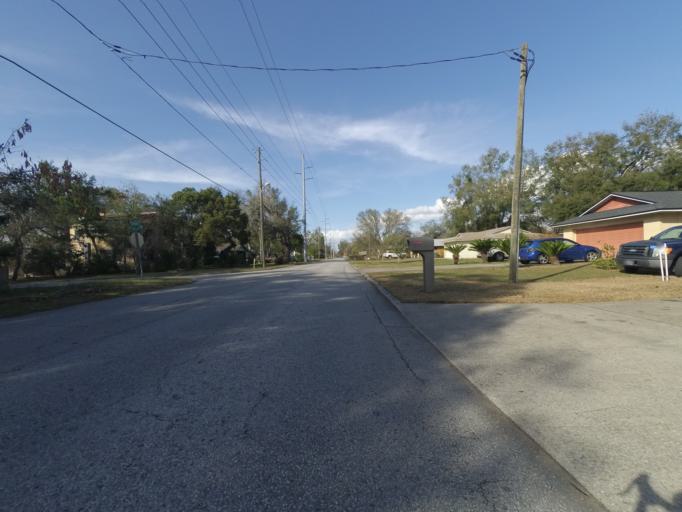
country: US
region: Florida
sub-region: Lake County
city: Eustis
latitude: 28.8382
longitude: -81.6835
